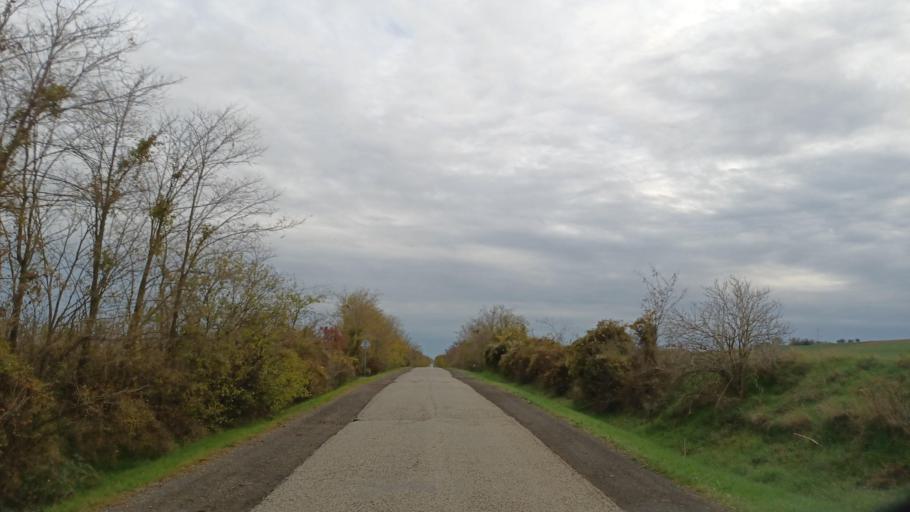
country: HU
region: Tolna
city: Simontornya
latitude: 46.6985
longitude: 18.5882
